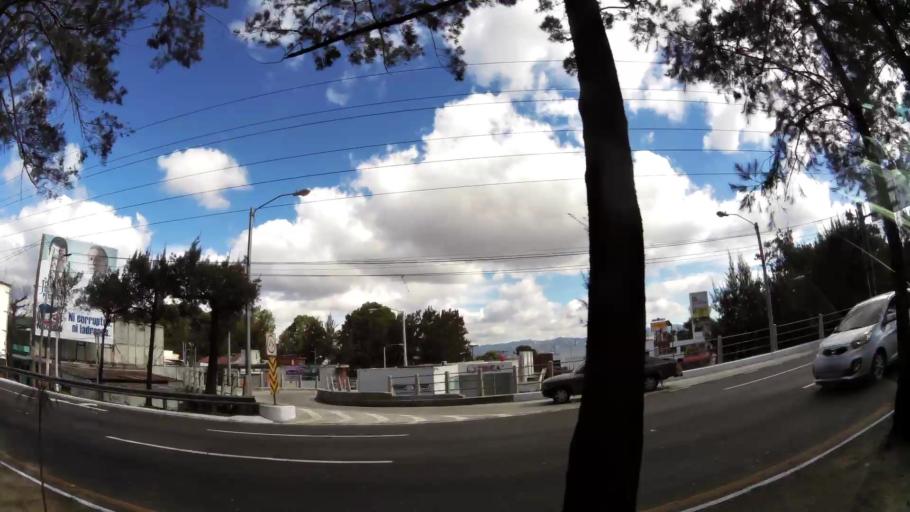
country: GT
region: Guatemala
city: Guatemala City
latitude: 14.6292
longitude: -90.5555
